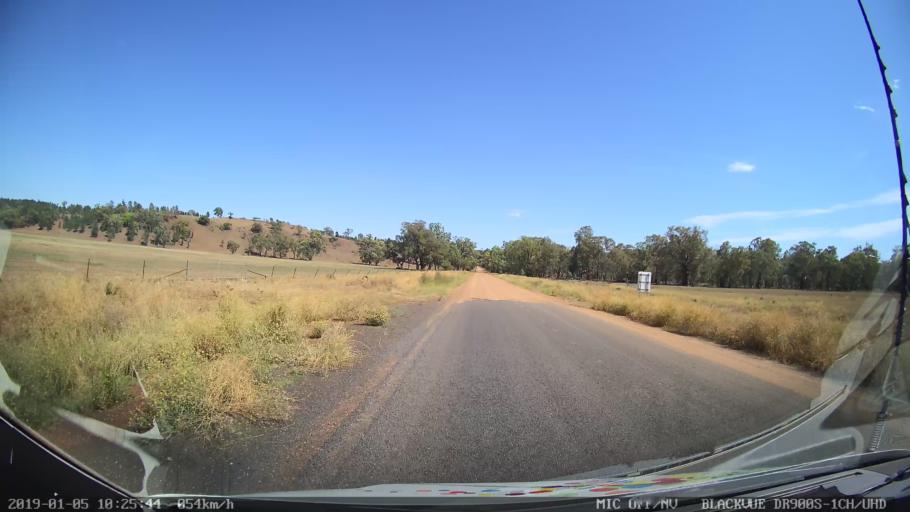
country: AU
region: New South Wales
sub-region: Gilgandra
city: Gilgandra
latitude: -31.5588
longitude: 148.9579
